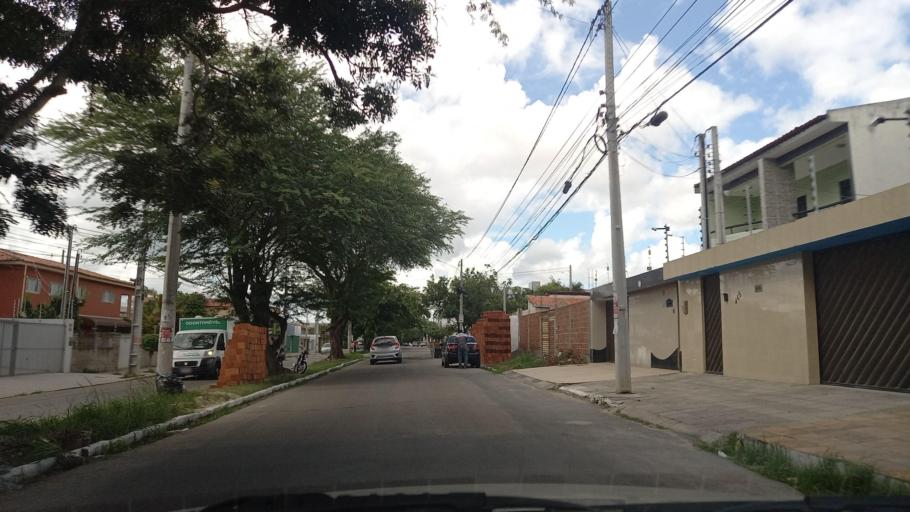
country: BR
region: Pernambuco
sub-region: Caruaru
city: Caruaru
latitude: -8.2969
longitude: -35.9770
